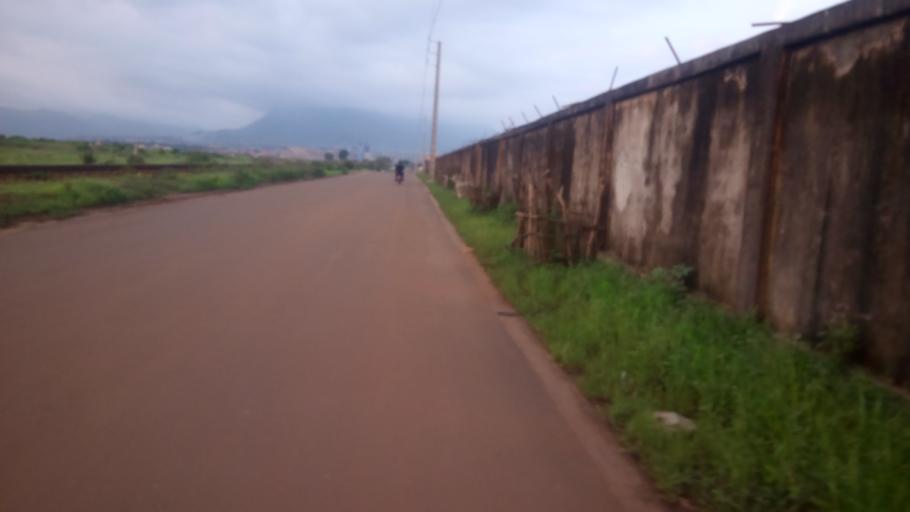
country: GN
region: Kindia
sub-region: Prefecture de Dubreka
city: Dubreka
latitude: 9.7182
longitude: -13.4957
